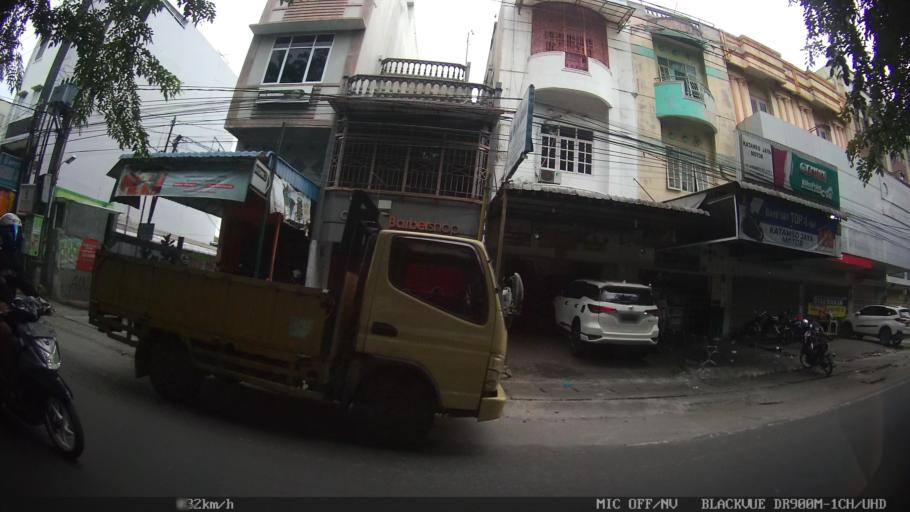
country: ID
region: North Sumatra
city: Medan
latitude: 3.5597
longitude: 98.6893
